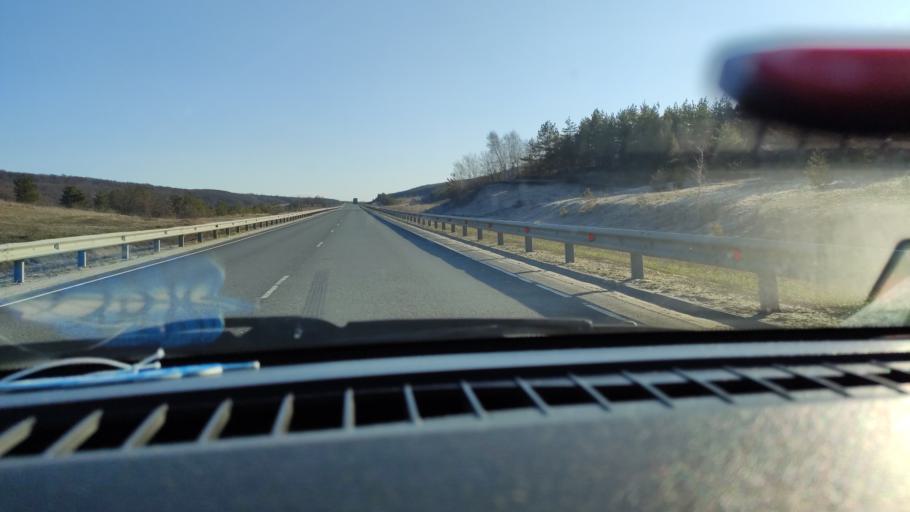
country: RU
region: Saratov
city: Alekseyevka
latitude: 52.4026
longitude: 47.9930
